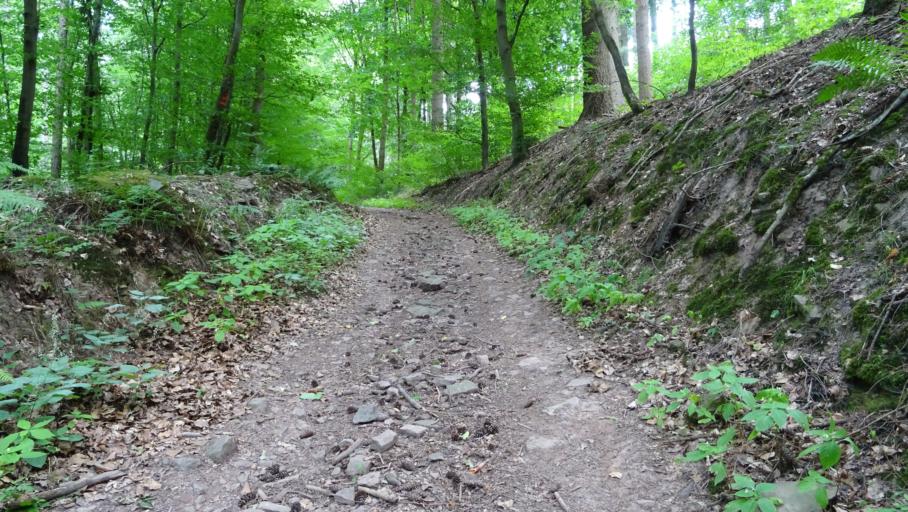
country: DE
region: Baden-Wuerttemberg
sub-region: Karlsruhe Region
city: Neckargerach
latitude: 49.3820
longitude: 9.0835
